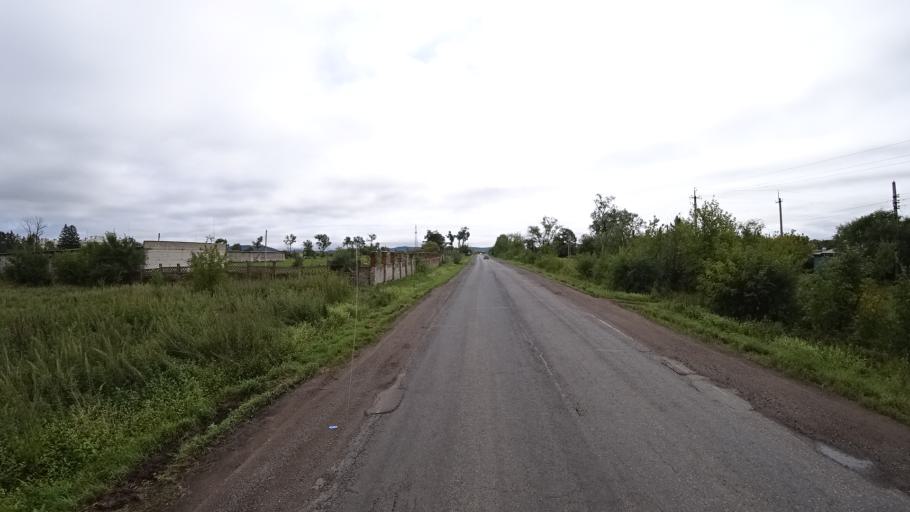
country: RU
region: Primorskiy
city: Monastyrishche
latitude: 44.2042
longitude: 132.4741
